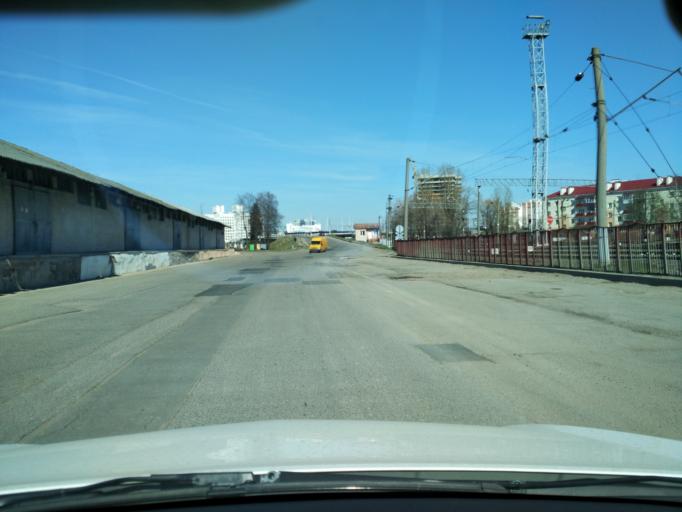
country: BY
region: Minsk
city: Minsk
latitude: 53.8814
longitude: 27.5315
